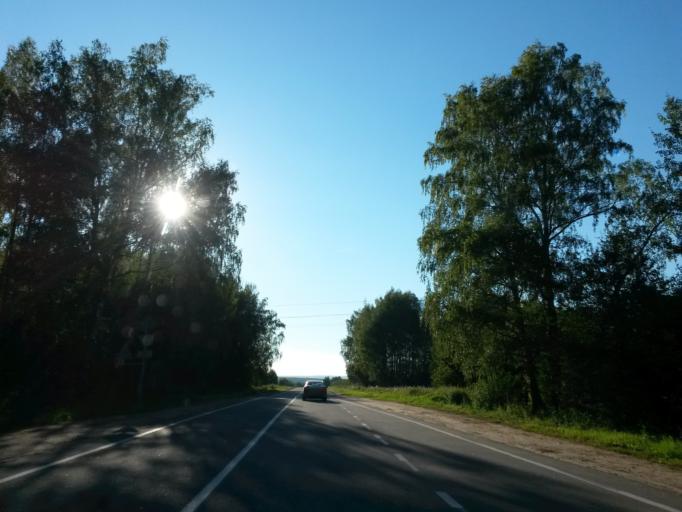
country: RU
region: Jaroslavl
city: Gavrilov-Yam
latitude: 57.2728
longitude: 39.9479
